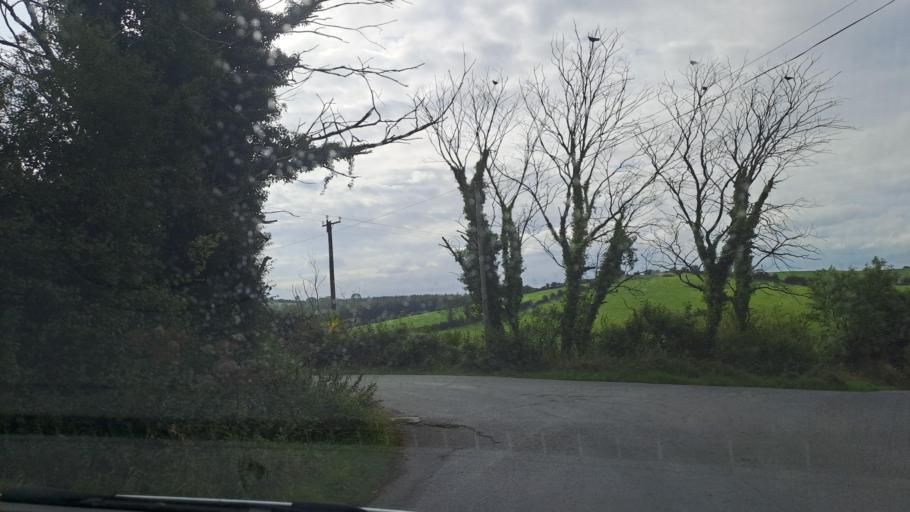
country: IE
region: Ulster
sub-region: An Cabhan
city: Kingscourt
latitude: 53.9885
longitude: -6.8617
